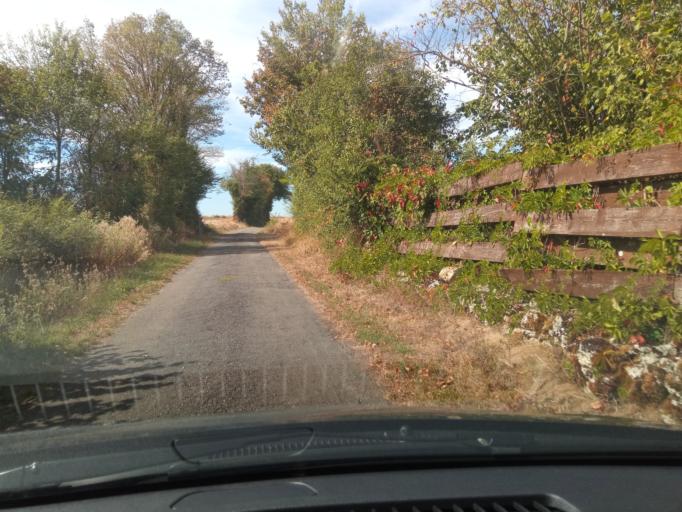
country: FR
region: Poitou-Charentes
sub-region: Departement de la Vienne
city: Chauvigny
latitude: 46.5560
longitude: 0.7433
